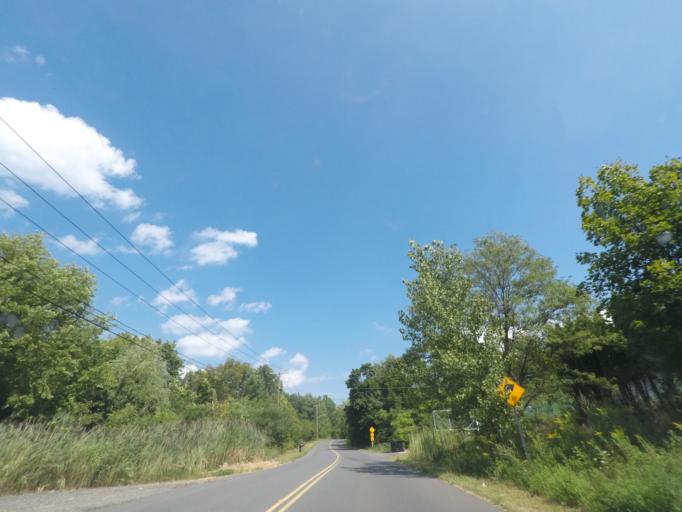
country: US
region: New York
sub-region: Saratoga County
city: Waterford
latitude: 42.7841
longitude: -73.6591
